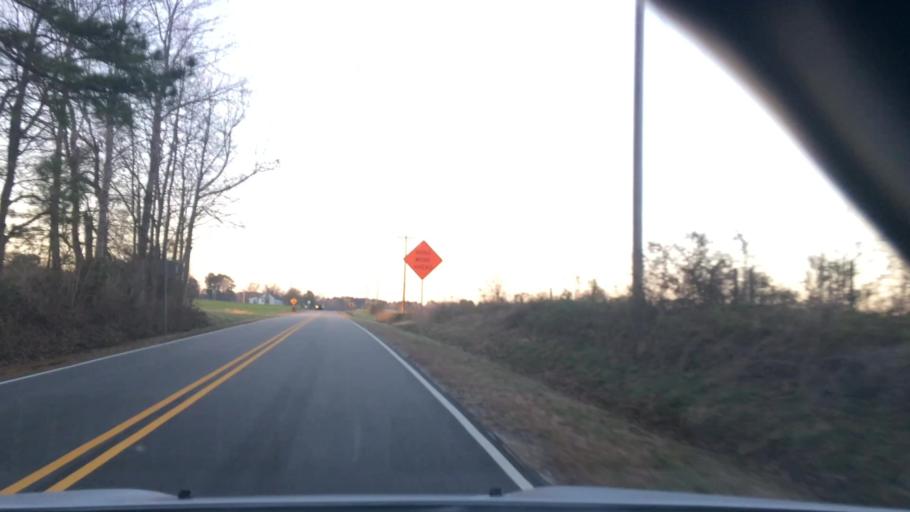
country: US
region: North Carolina
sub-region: Wake County
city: Rolesville
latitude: 35.9547
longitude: -78.4111
